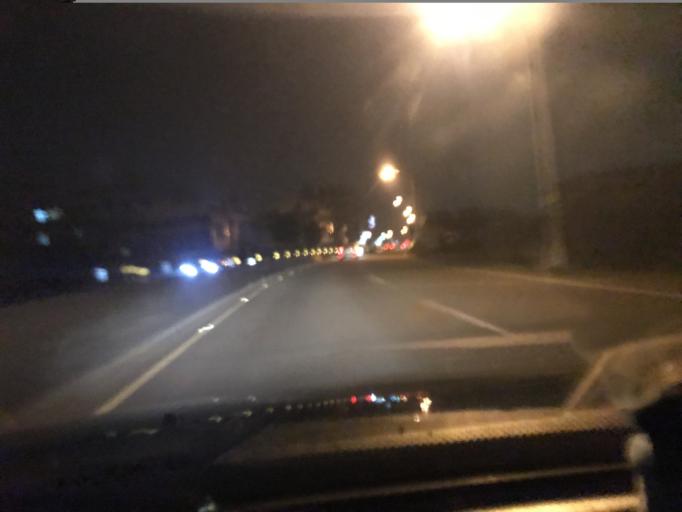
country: TW
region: Taiwan
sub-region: Hsinchu
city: Zhubei
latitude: 24.7970
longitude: 121.0553
